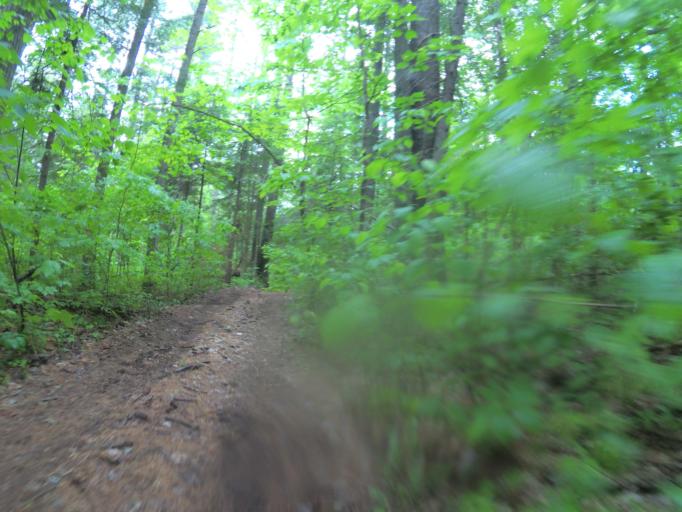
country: CA
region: Ontario
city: Renfrew
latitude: 45.1297
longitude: -76.8332
